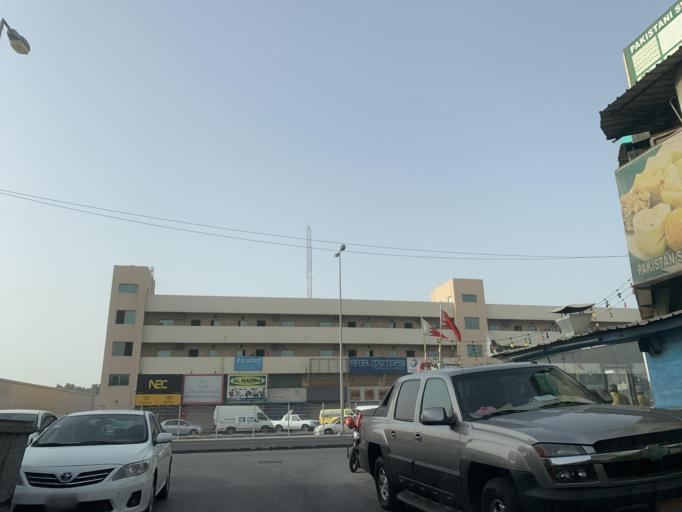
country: BH
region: Northern
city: Madinat `Isa
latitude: 26.1861
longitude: 50.5298
